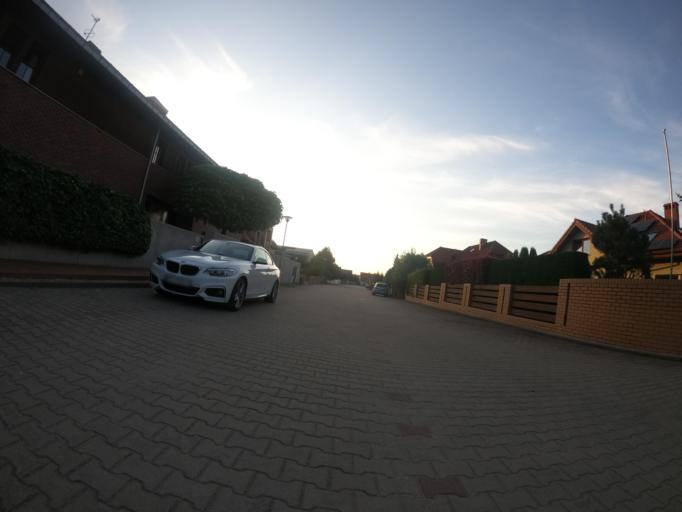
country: PL
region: West Pomeranian Voivodeship
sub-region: Powiat policki
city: Dobra
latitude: 53.4564
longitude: 14.4518
